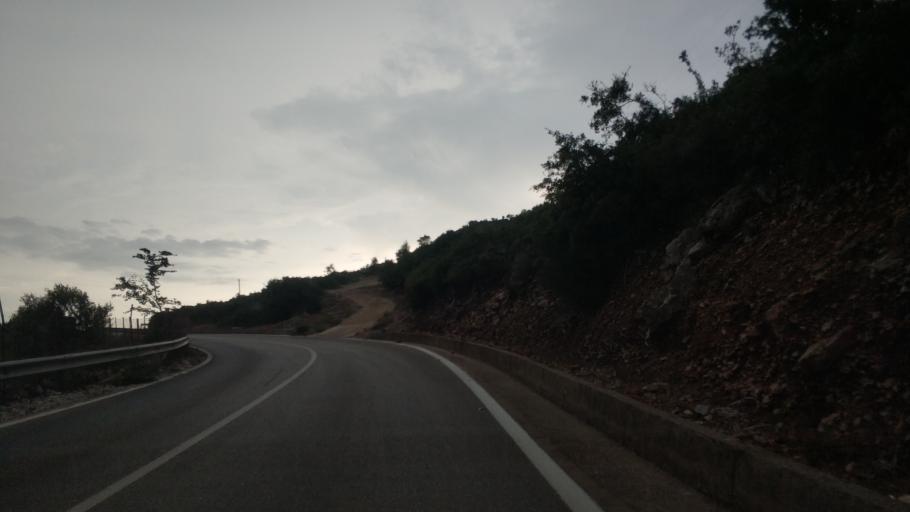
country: AL
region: Vlore
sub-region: Rrethi i Sarandes
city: Lukove
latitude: 40.0590
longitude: 19.8475
